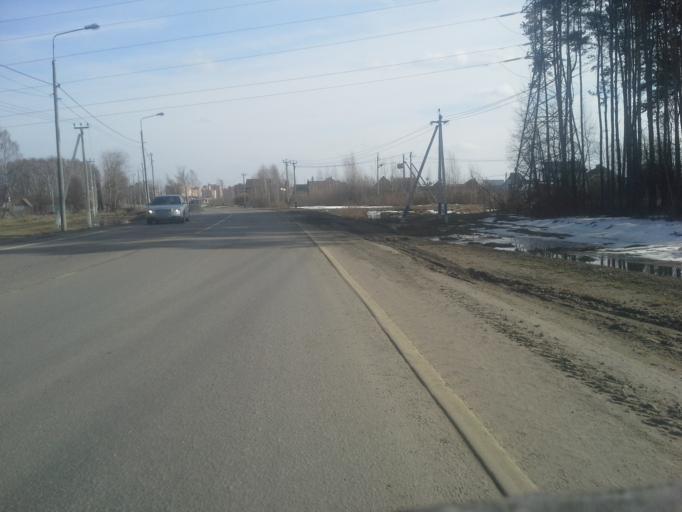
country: RU
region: Moskovskaya
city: Shcherbinka
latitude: 55.4809
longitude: 37.5230
